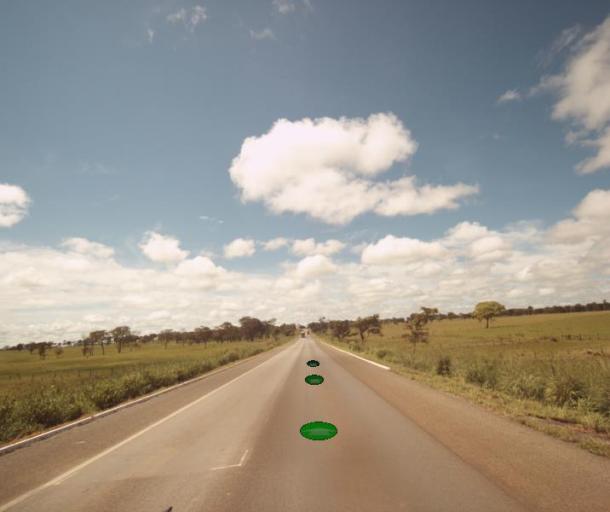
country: BR
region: Goias
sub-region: Padre Bernardo
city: Padre Bernardo
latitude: -15.1605
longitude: -48.3111
